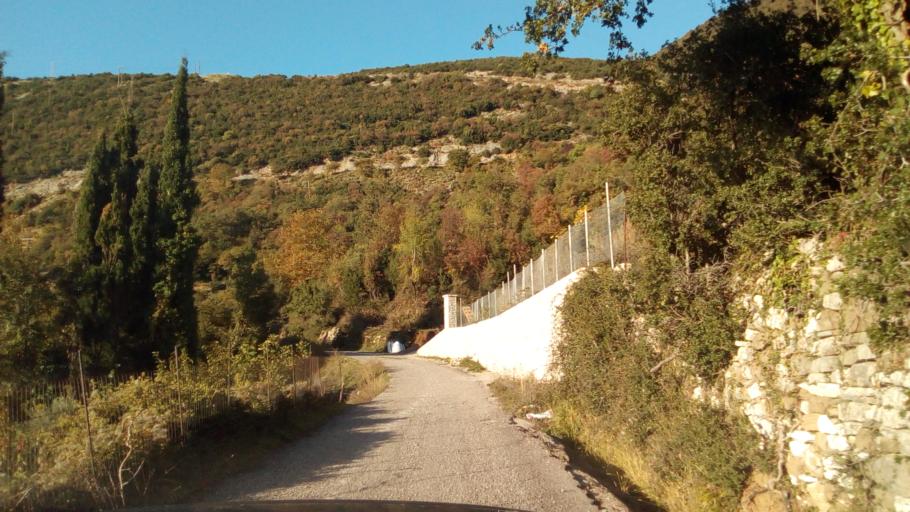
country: GR
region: West Greece
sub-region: Nomos Aitolias kai Akarnanias
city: Thermo
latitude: 38.5909
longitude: 21.7978
